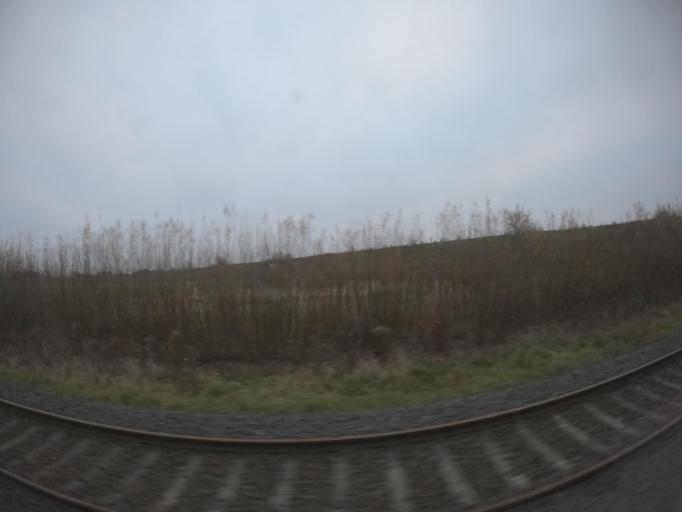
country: PL
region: Lubusz
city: Gorzow Wielkopolski
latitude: 52.7123
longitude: 15.1672
